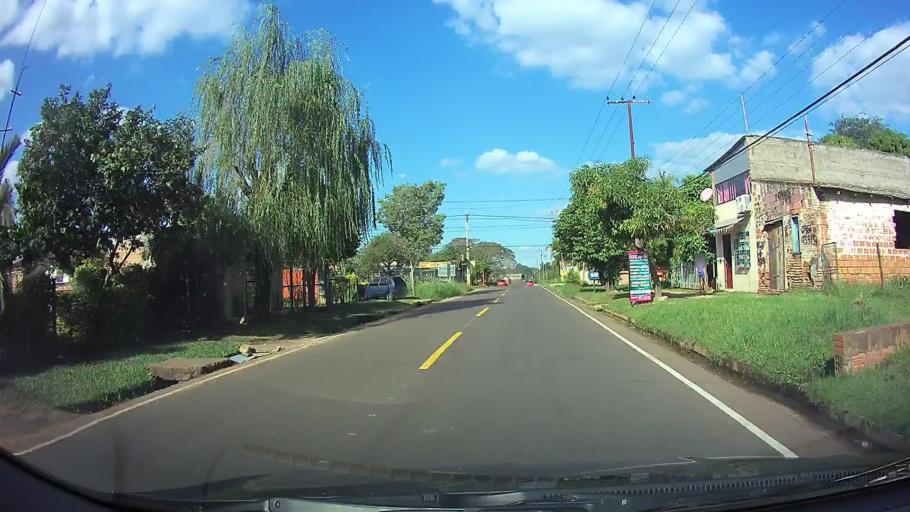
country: PY
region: Central
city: San Lorenzo
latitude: -25.2666
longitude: -57.4715
